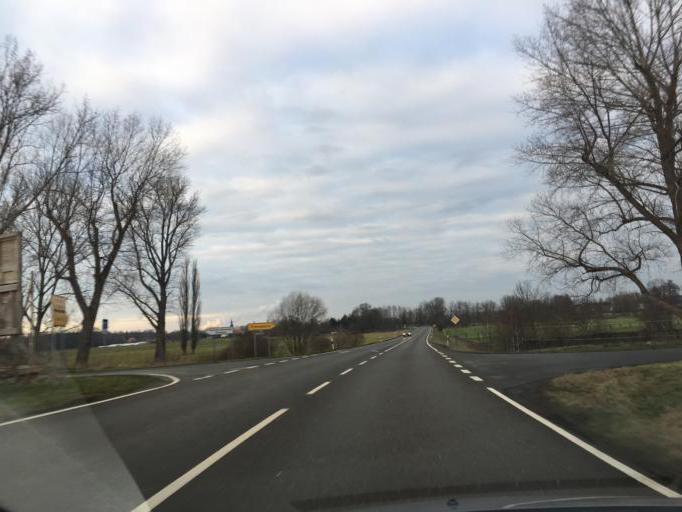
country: DE
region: Thuringia
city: Fockendorf
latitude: 51.0432
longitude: 12.4554
